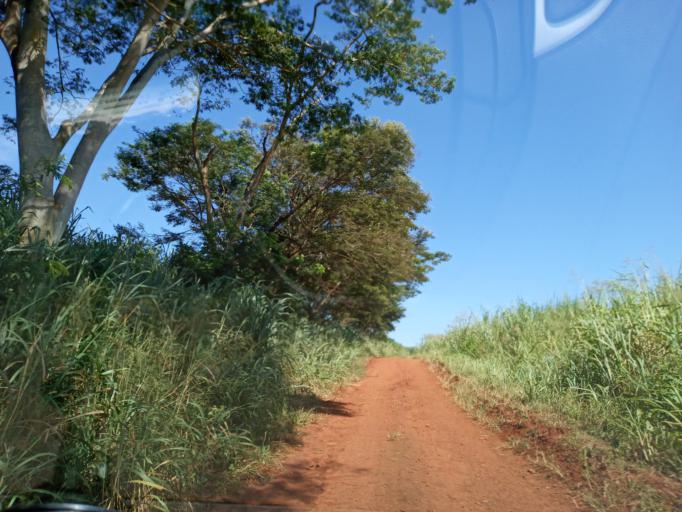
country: BR
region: Goias
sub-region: Itumbiara
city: Itumbiara
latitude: -18.4525
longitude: -49.1427
